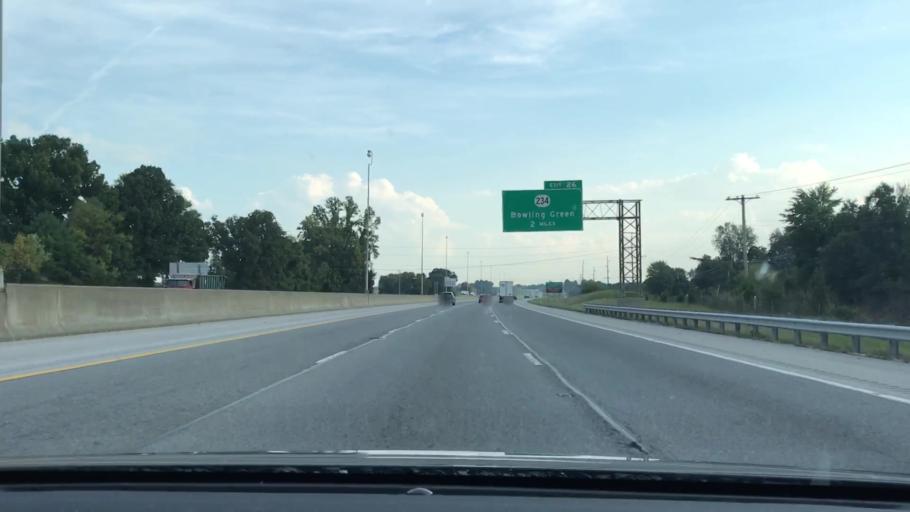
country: US
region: Kentucky
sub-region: Warren County
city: Bowling Green
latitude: 36.9478
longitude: -86.4102
